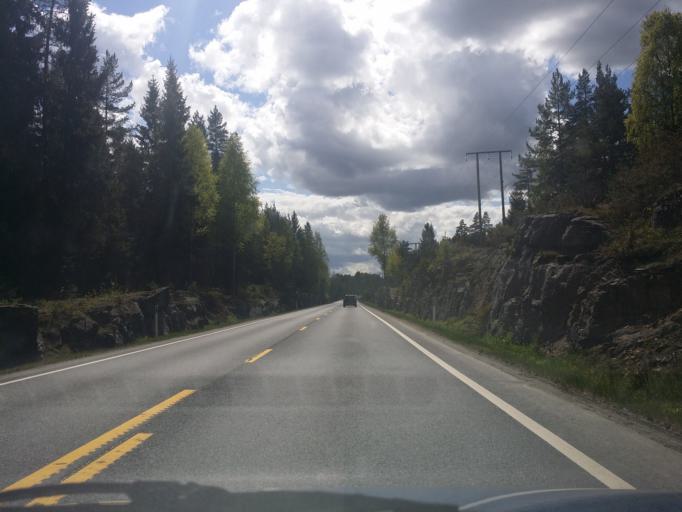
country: NO
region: Buskerud
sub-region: Modum
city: Vikersund
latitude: 59.9553
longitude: 9.9761
